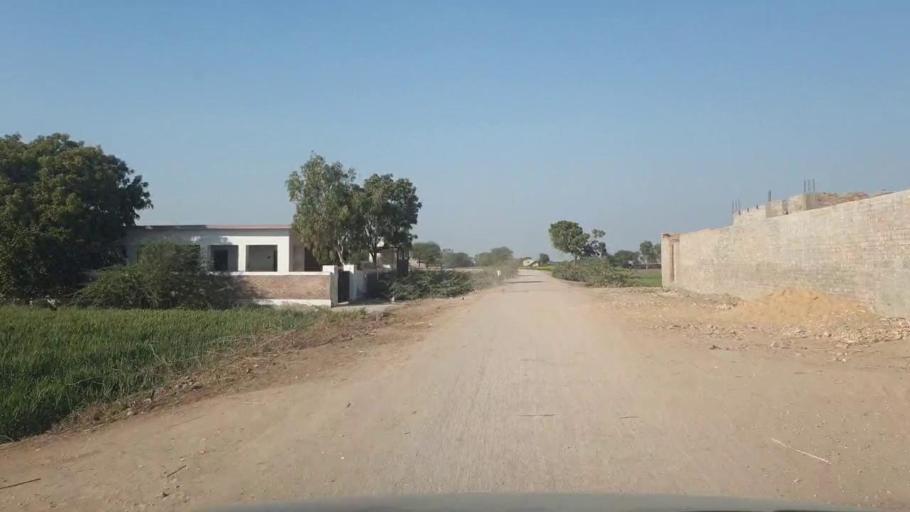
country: PK
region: Sindh
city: Chambar
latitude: 25.2896
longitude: 68.8646
